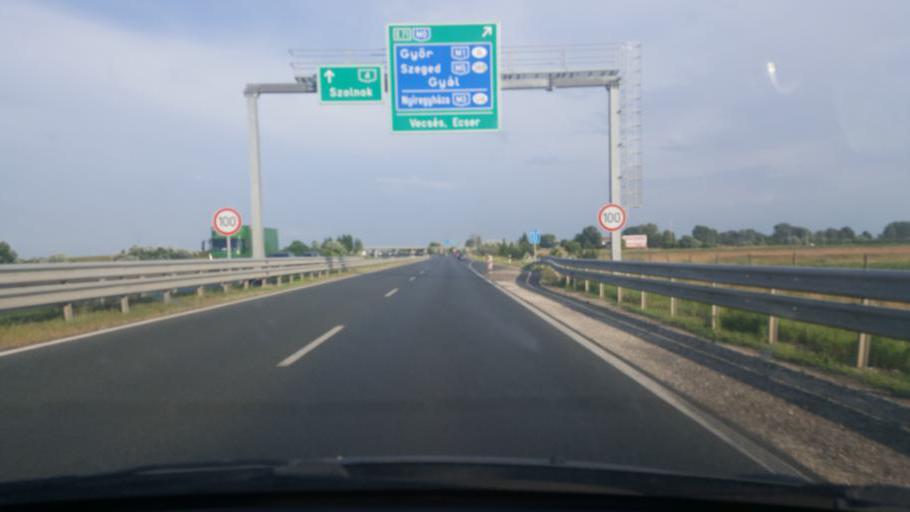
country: HU
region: Pest
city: Vecses
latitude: 47.4084
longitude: 19.2983
